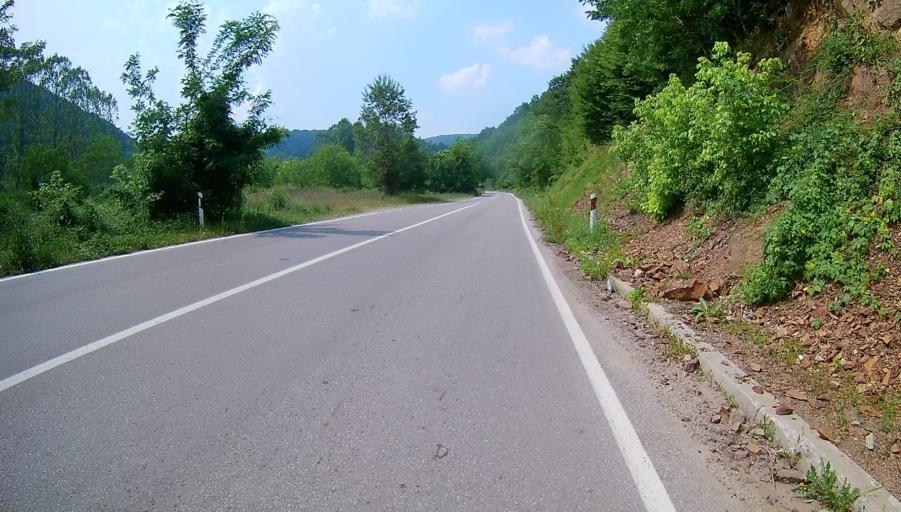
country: RS
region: Central Serbia
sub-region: Nisavski Okrug
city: Gadzin Han
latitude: 43.1788
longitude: 22.0470
